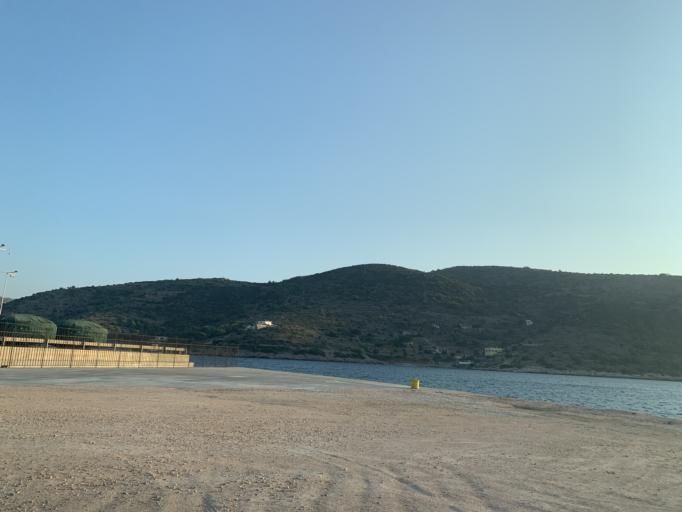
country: GR
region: North Aegean
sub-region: Chios
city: Thymiana
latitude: 38.2922
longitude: 25.9289
